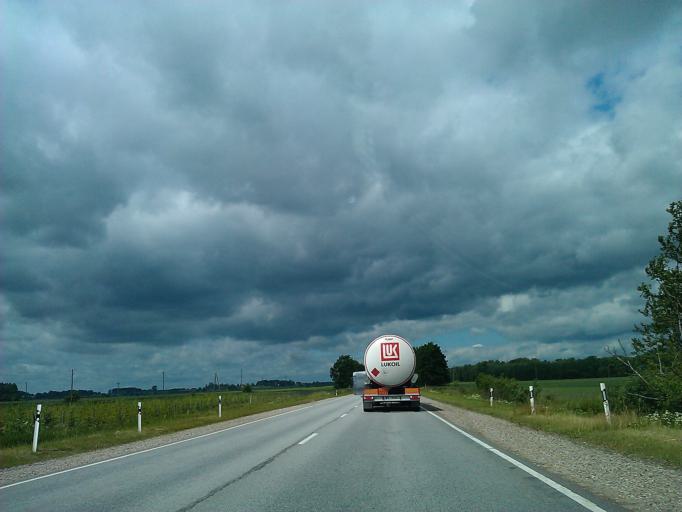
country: LV
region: Engure
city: Smarde
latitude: 56.9187
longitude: 23.3100
